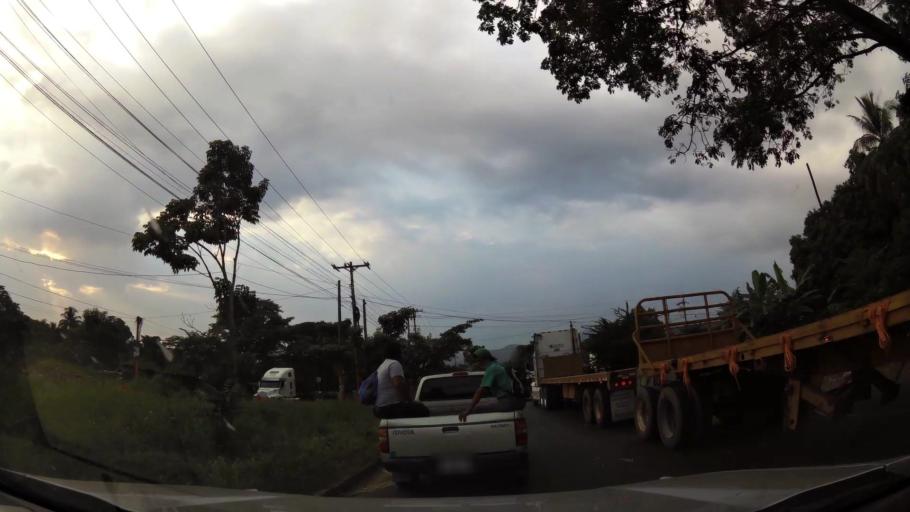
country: GT
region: Escuintla
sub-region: Municipio de Escuintla
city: Escuintla
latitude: 14.2830
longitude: -90.7884
